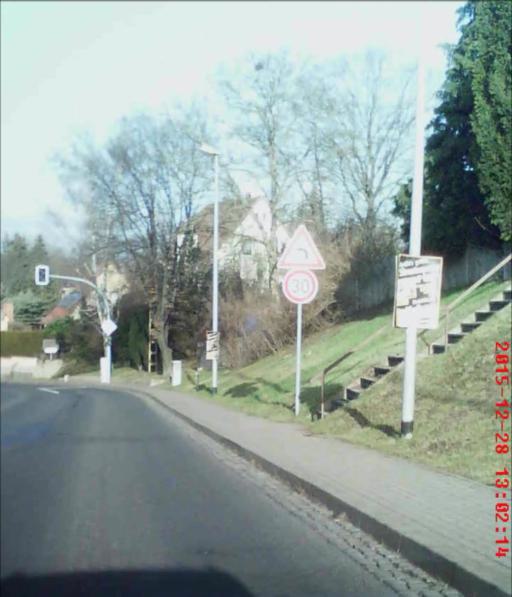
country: DE
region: Thuringia
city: Niederrossla
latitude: 51.0363
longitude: 11.4889
